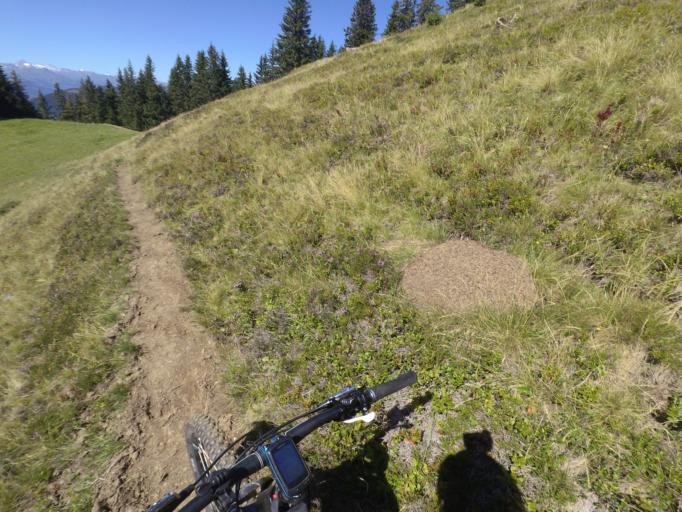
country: AT
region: Salzburg
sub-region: Politischer Bezirk Sankt Johann im Pongau
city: Goldegg
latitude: 47.3484
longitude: 13.0673
